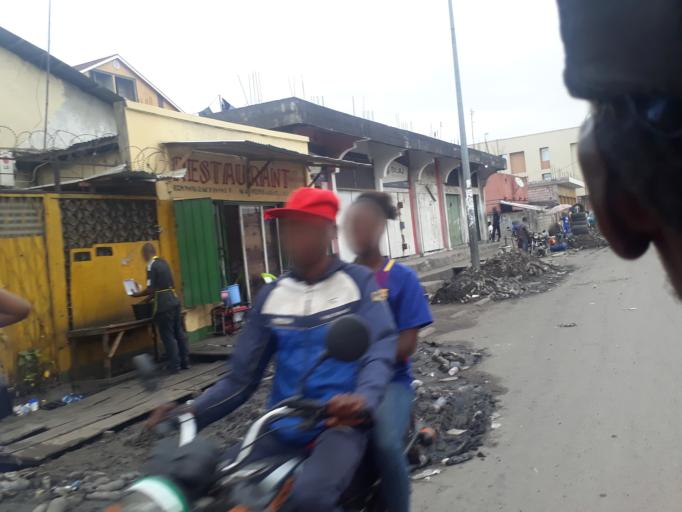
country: CD
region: Kinshasa
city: Kinshasa
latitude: -4.3166
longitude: 15.3105
